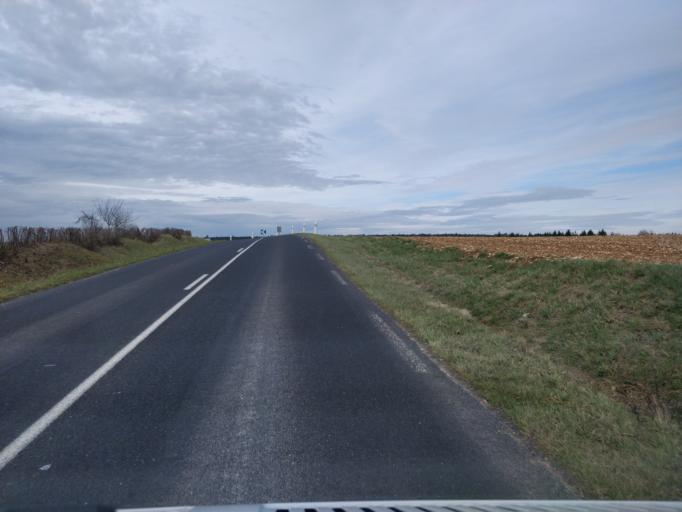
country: FR
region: Lorraine
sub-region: Departement de Meurthe-et-Moselle
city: Montauville
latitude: 48.9080
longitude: 5.9396
